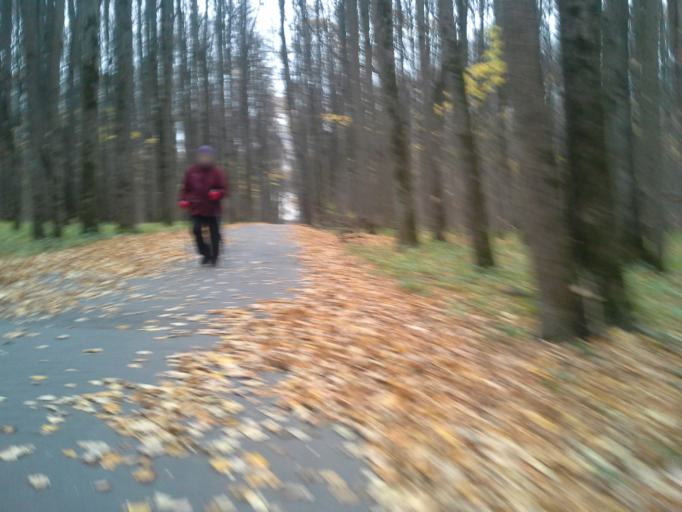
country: RU
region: Moscow
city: Zyuzino
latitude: 55.6252
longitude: 37.5769
